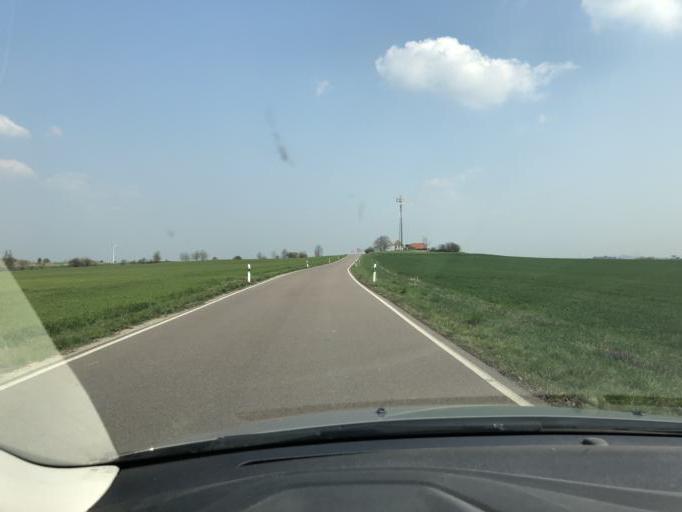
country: DE
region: Saxony-Anhalt
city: Niemberg
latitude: 51.5629
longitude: 12.0680
